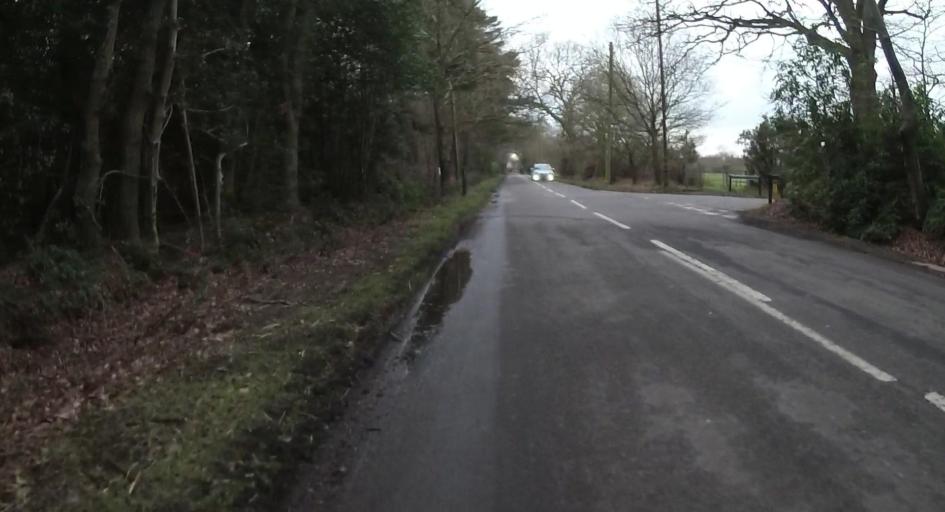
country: GB
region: England
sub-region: West Berkshire
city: Stratfield Mortimer
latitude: 51.3793
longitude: -1.0570
